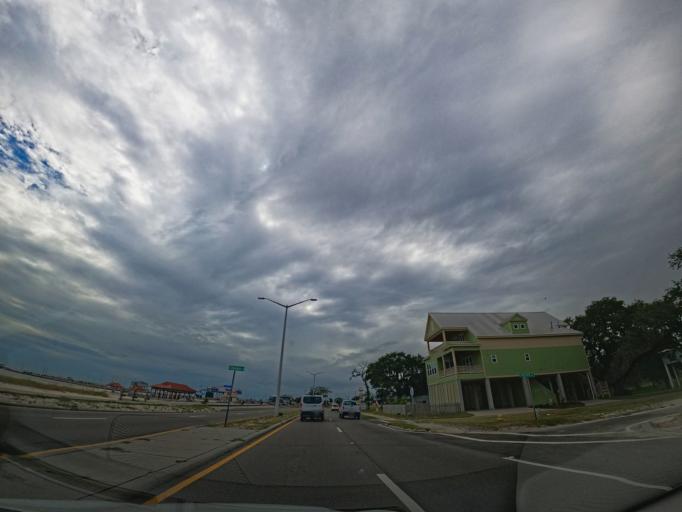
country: US
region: Mississippi
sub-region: Harrison County
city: Long Beach
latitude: 30.3480
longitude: -89.1405
